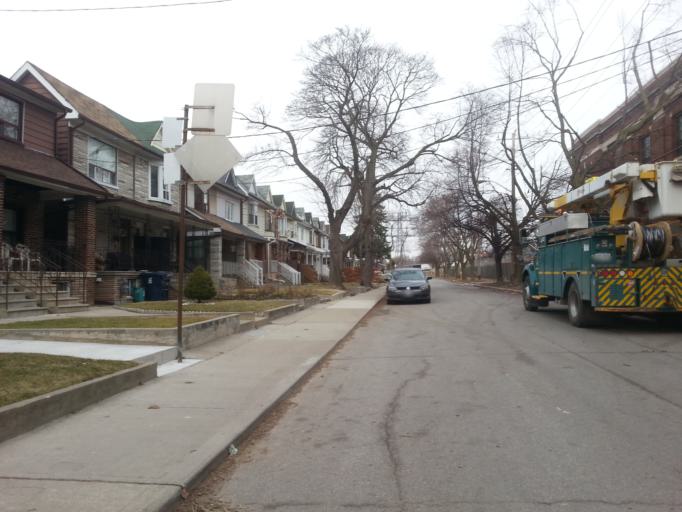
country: CA
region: Ontario
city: Toronto
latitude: 43.6688
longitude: -79.4513
